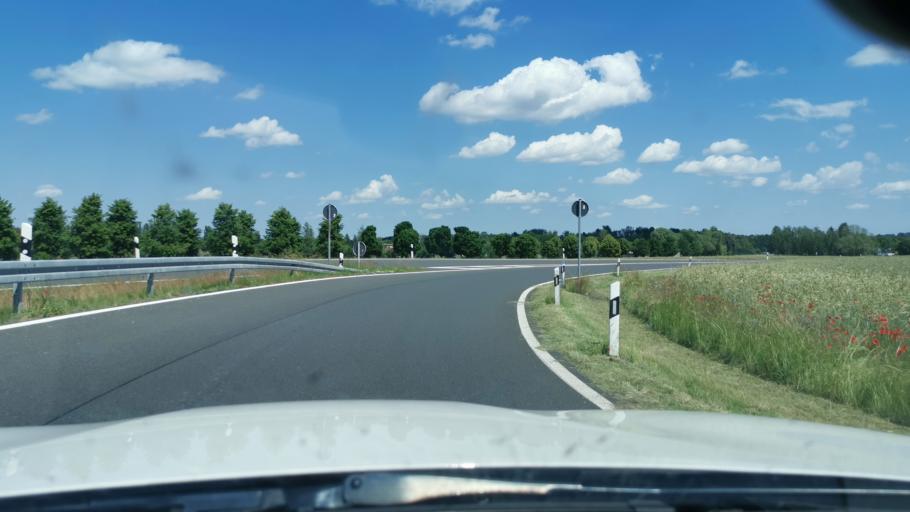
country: DE
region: Brandenburg
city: Werder
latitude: 52.4115
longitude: 12.8965
